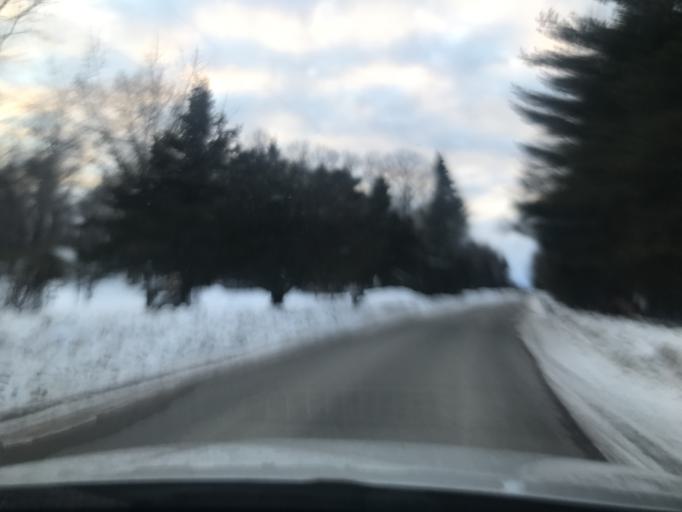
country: US
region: Wisconsin
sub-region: Marinette County
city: Peshtigo
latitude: 45.1642
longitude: -87.7273
